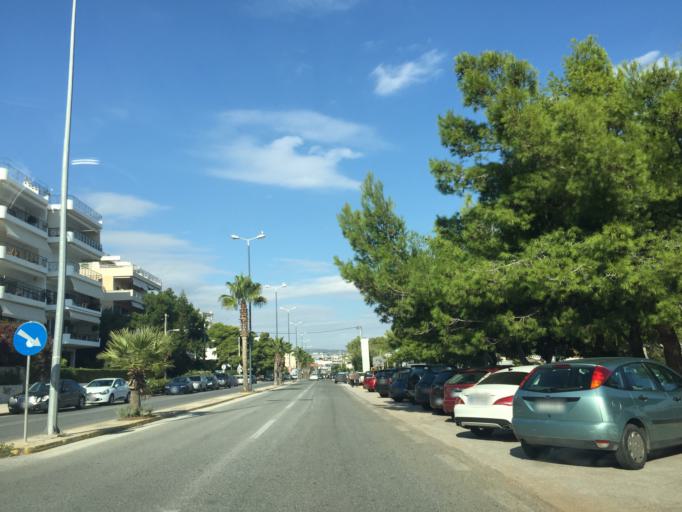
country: GR
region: Attica
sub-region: Nomarchia Anatolikis Attikis
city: Vari
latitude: 37.8153
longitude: 23.8009
